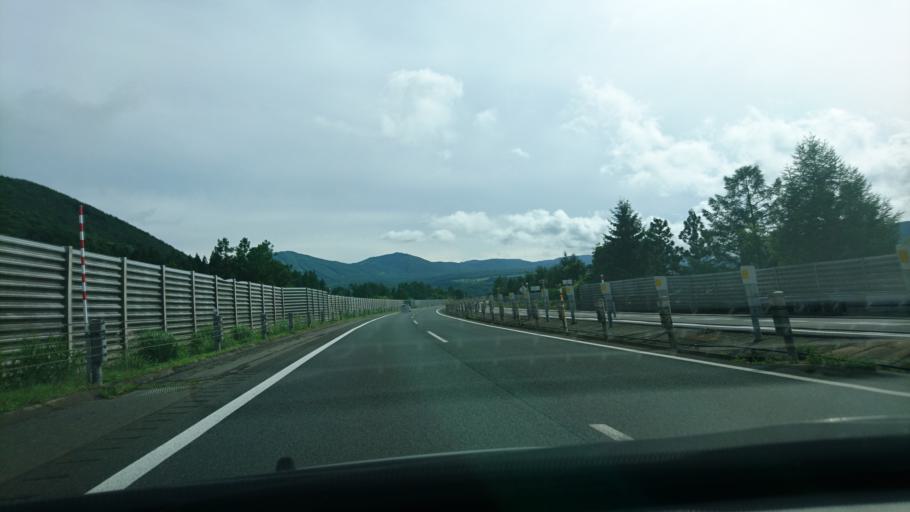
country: JP
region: Akita
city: Hanawa
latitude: 40.0360
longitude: 140.9893
